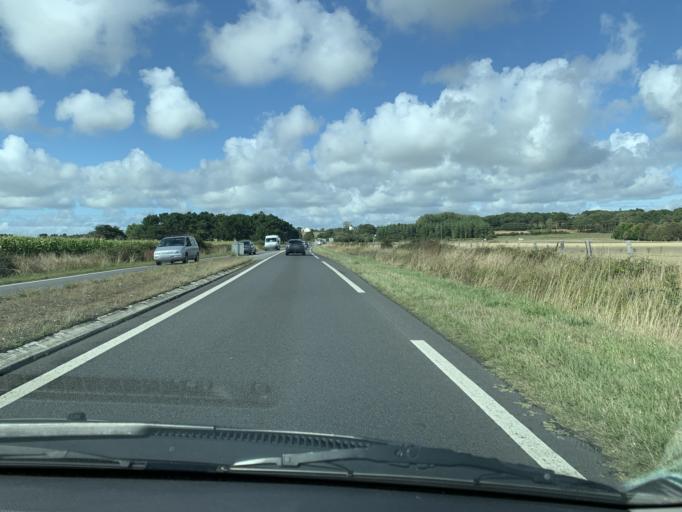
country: FR
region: Pays de la Loire
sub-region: Departement de la Loire-Atlantique
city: Guerande
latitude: 47.3108
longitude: -2.4295
